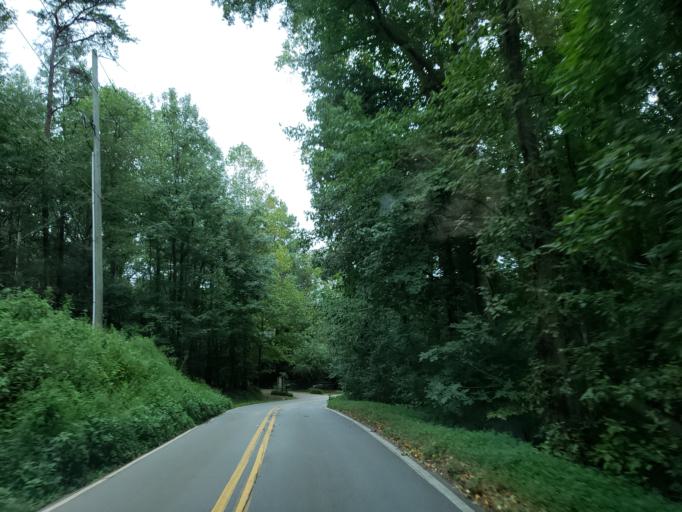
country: US
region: Georgia
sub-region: Pickens County
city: Jasper
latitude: 34.4297
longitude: -84.5507
